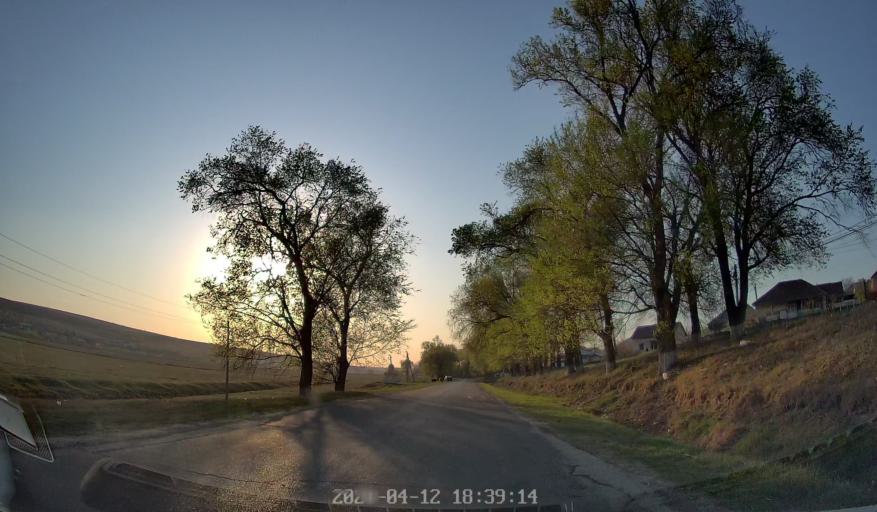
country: MD
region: Chisinau
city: Vadul lui Voda
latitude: 47.1273
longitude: 28.9889
